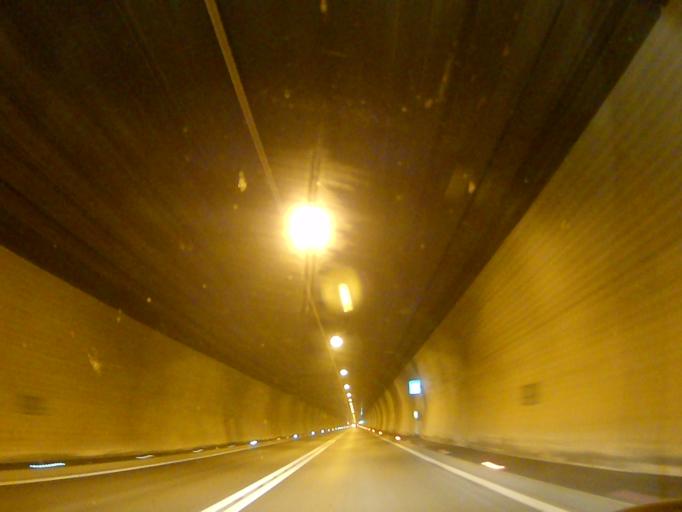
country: AT
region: Tyrol
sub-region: Politischer Bezirk Landeck
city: Zams
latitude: 47.1656
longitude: 10.6099
